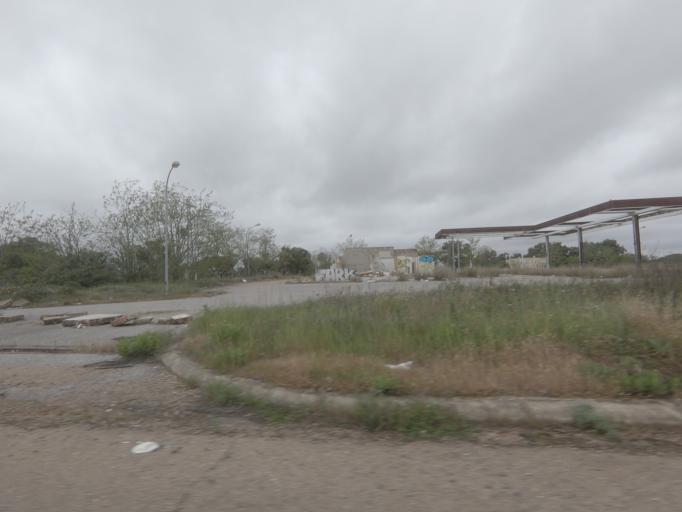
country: ES
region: Extremadura
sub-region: Provincia de Badajoz
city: Villar del Rey
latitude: 38.9934
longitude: -6.8724
